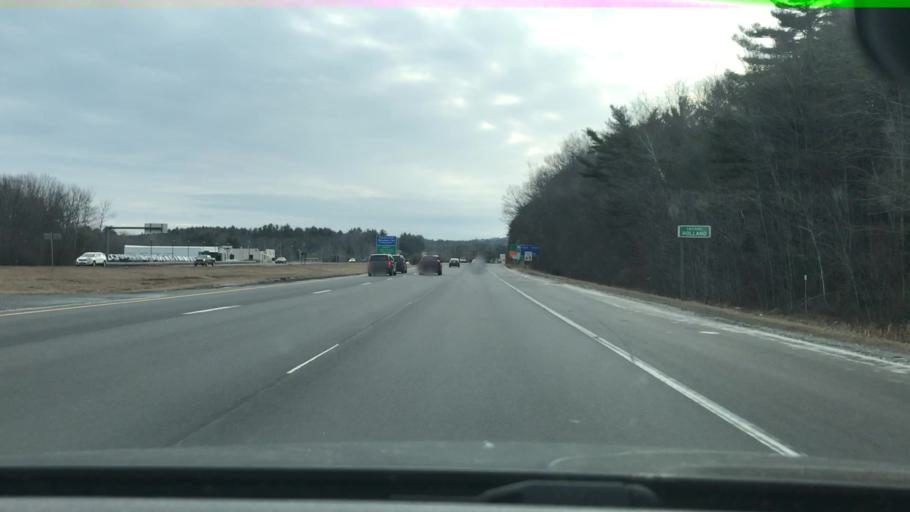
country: US
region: Massachusetts
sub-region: Hampden County
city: Holland
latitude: 42.0317
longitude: -72.1356
